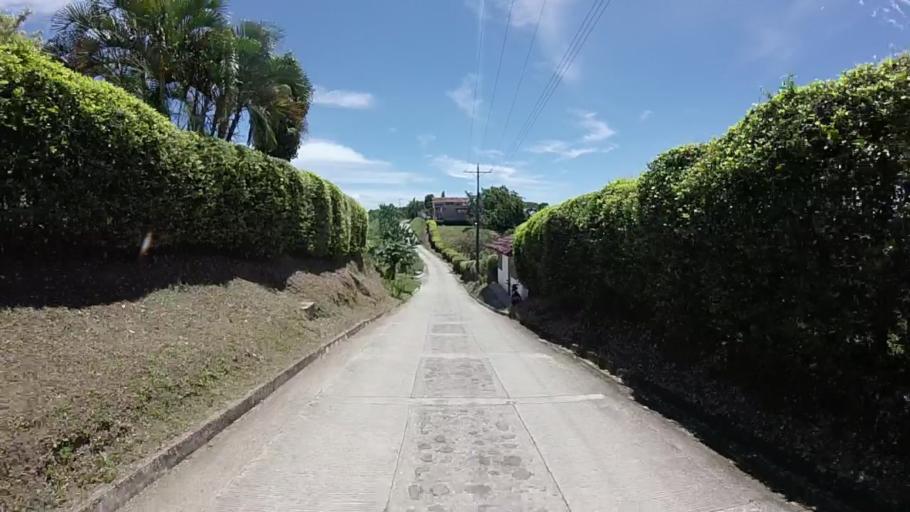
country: CO
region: Valle del Cauca
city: Ulloa
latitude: 4.7131
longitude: -75.7699
